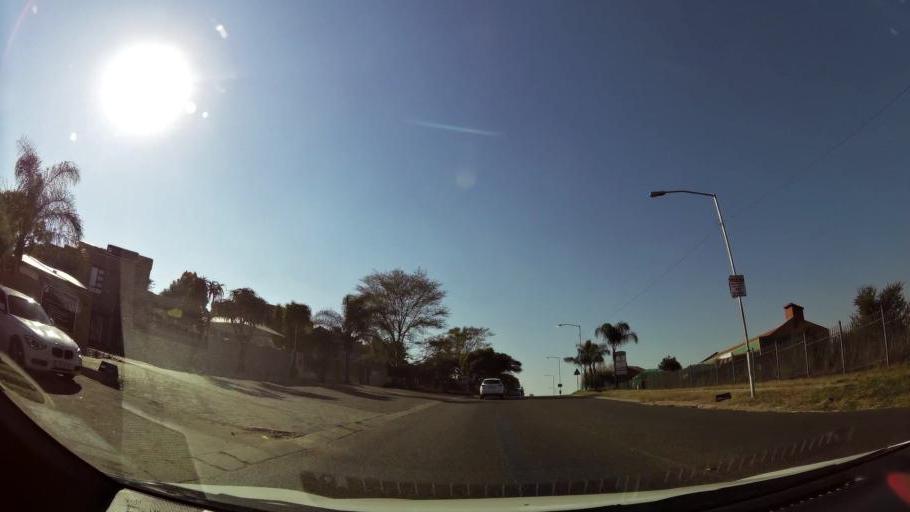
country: ZA
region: Gauteng
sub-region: City of Tshwane Metropolitan Municipality
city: Centurion
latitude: -25.8115
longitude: 28.2959
